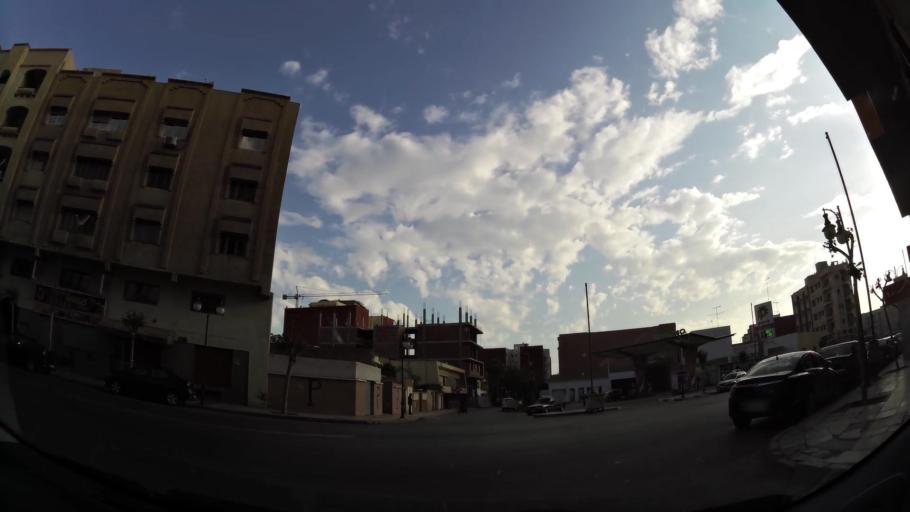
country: MA
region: Oriental
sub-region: Oujda-Angad
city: Oujda
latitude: 34.6757
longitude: -1.9243
